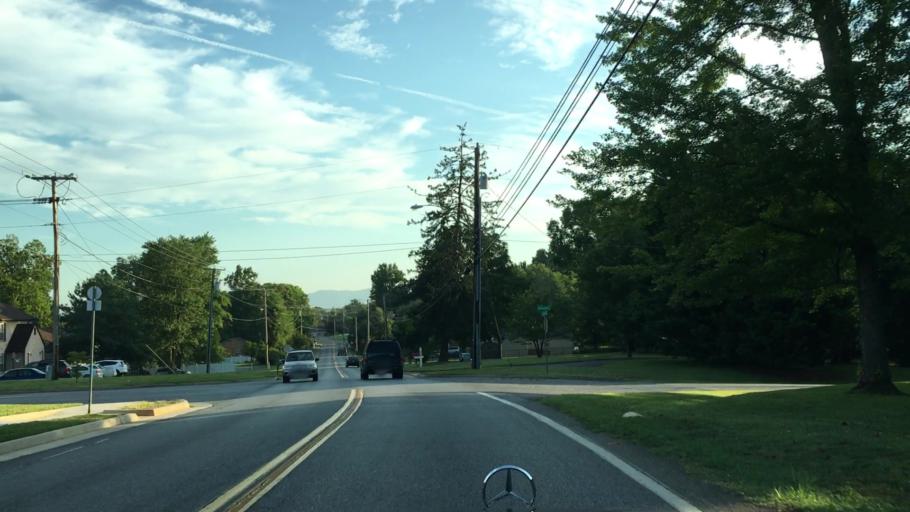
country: US
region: Virginia
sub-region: Campbell County
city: Timberlake
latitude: 37.3662
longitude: -79.2267
